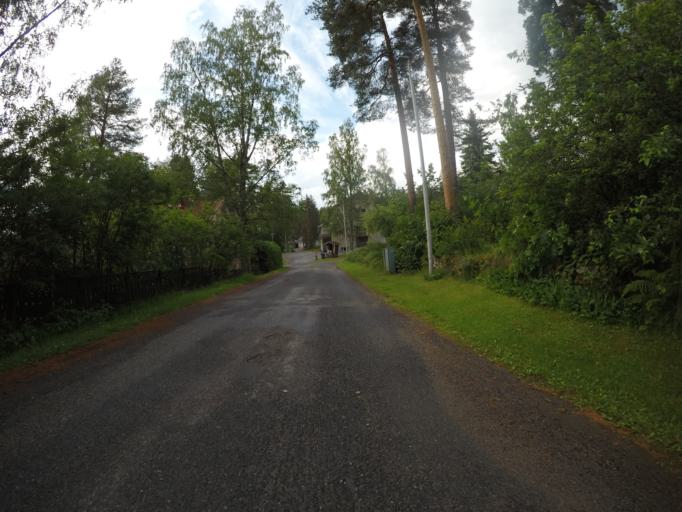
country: FI
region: Haeme
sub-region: Haemeenlinna
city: Haemeenlinna
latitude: 61.0128
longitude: 24.4799
